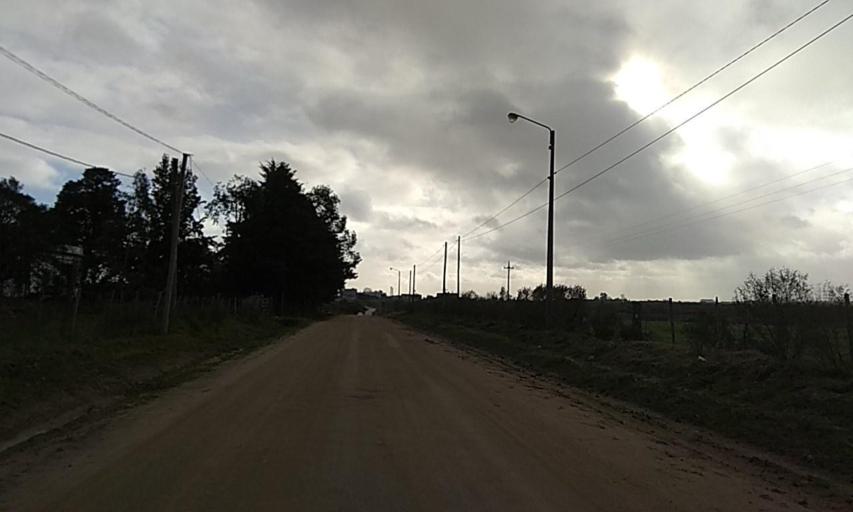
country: UY
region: Florida
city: Florida
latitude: -34.0737
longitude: -56.1975
